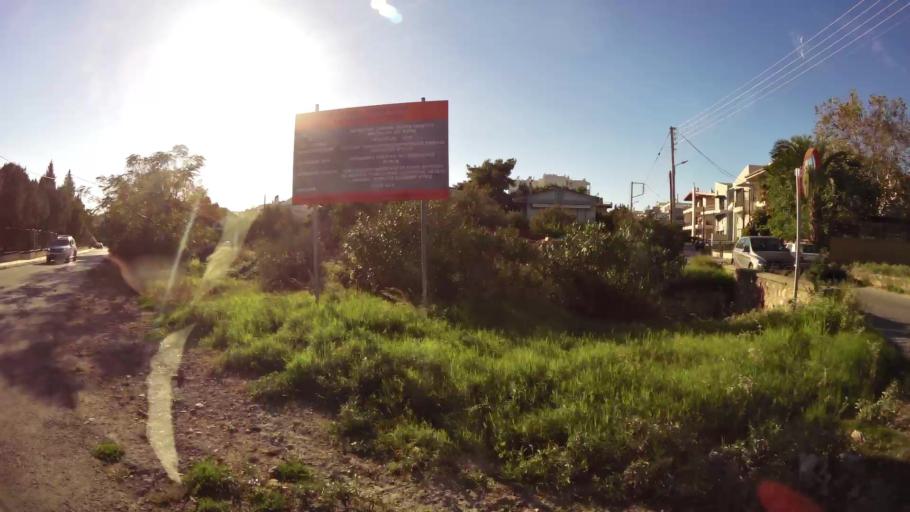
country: GR
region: Attica
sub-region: Nomarchia Anatolikis Attikis
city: Vari
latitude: 37.8325
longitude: 23.8063
